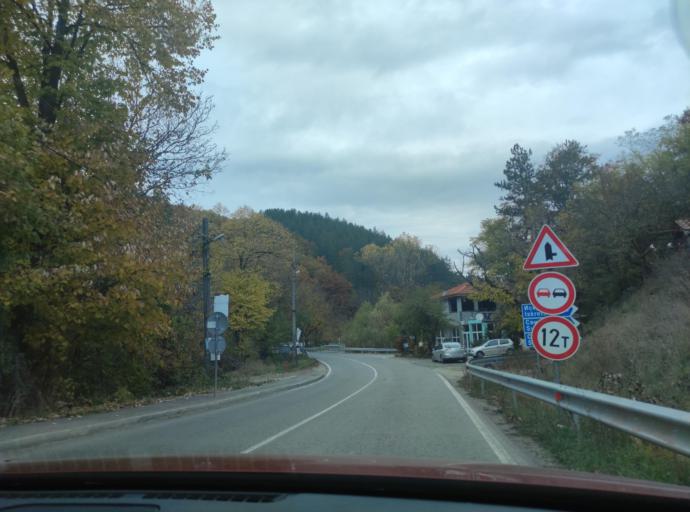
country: BG
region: Sofiya
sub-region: Obshtina Godech
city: Godech
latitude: 42.9750
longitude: 23.1387
